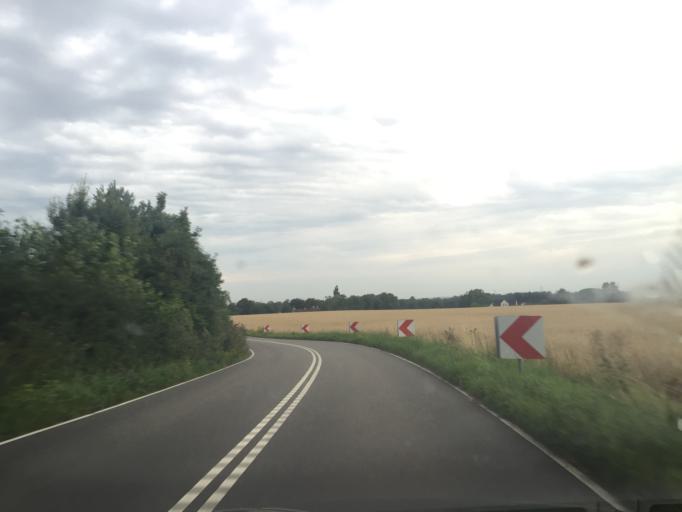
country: DK
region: Capital Region
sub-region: Egedal Kommune
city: Vekso
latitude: 55.7238
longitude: 12.2061
